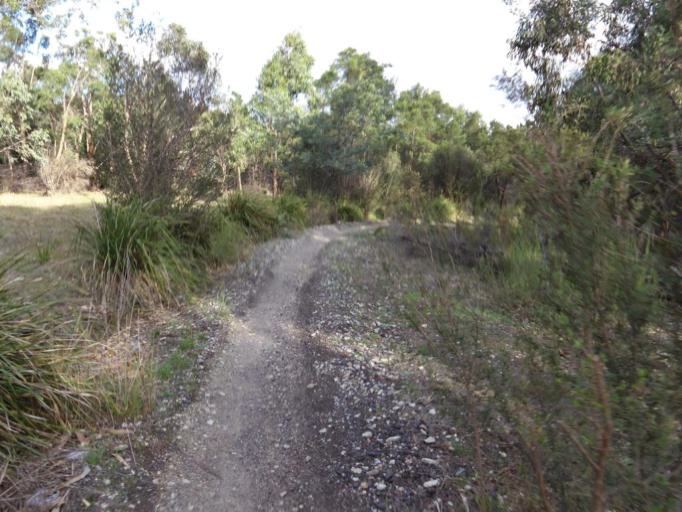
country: AU
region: Victoria
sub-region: Yarra Ranges
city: Lysterfield
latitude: -37.9499
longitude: 145.2799
